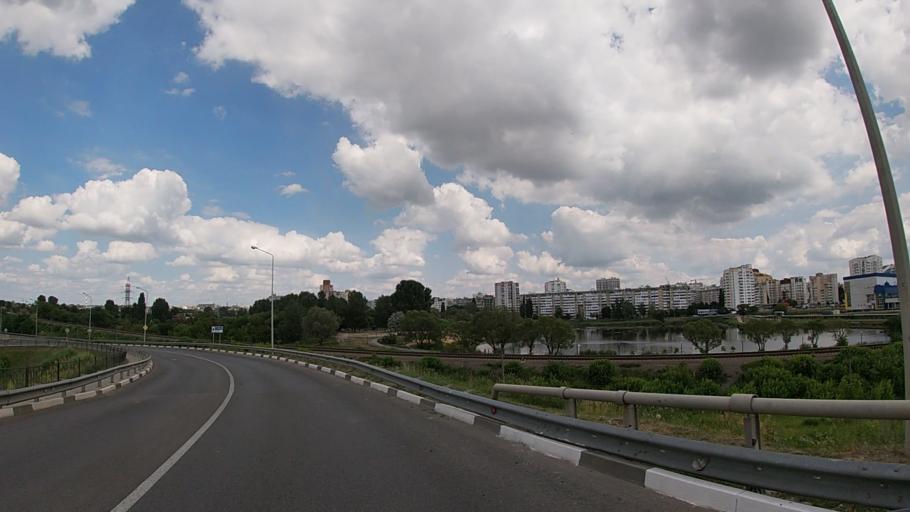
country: RU
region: Belgorod
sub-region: Belgorodskiy Rayon
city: Belgorod
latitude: 50.5906
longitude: 36.5655
